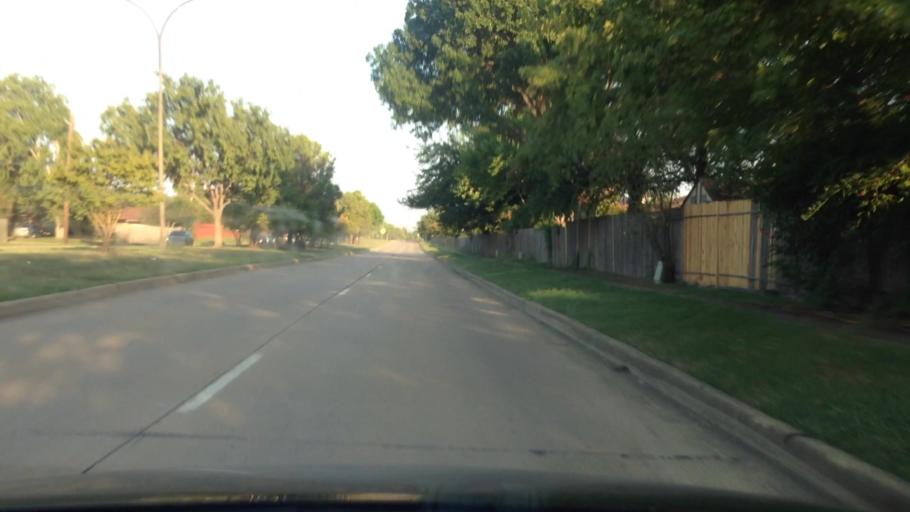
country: US
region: Texas
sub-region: Tarrant County
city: Dalworthington Gardens
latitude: 32.6591
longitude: -97.1106
